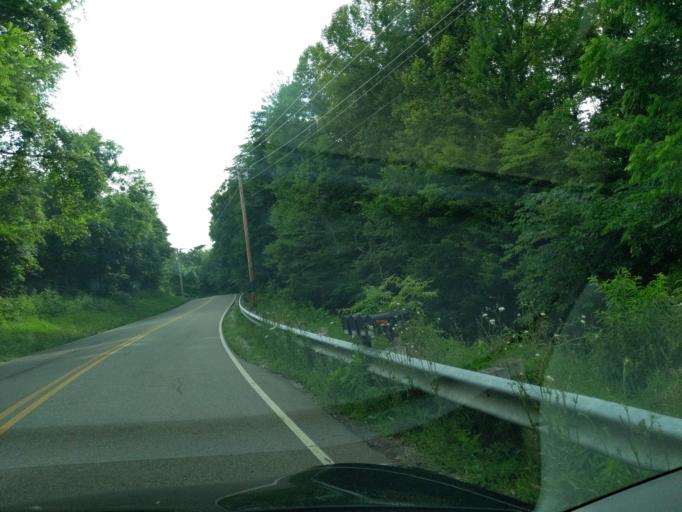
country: US
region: Ohio
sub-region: Fairfield County
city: Lancaster
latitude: 39.5664
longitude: -82.5935
